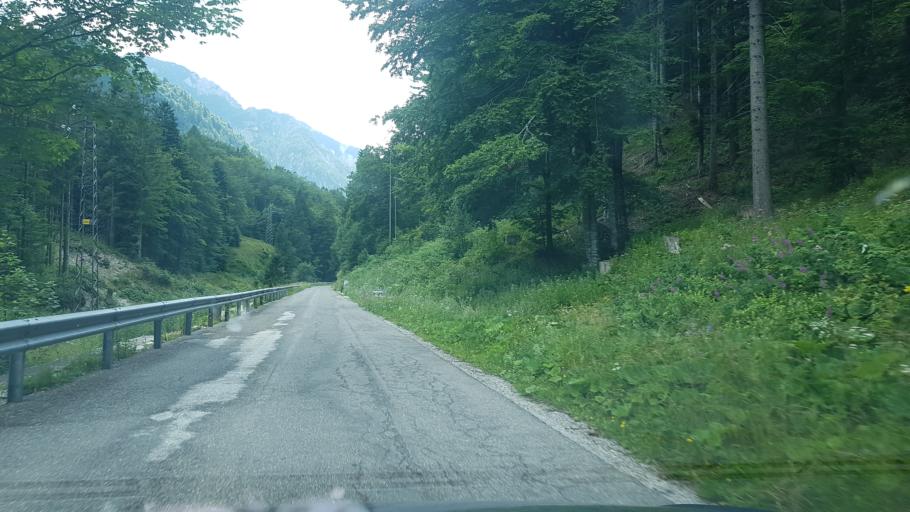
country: IT
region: Friuli Venezia Giulia
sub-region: Provincia di Udine
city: Pontebba
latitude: 46.5014
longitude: 13.2374
